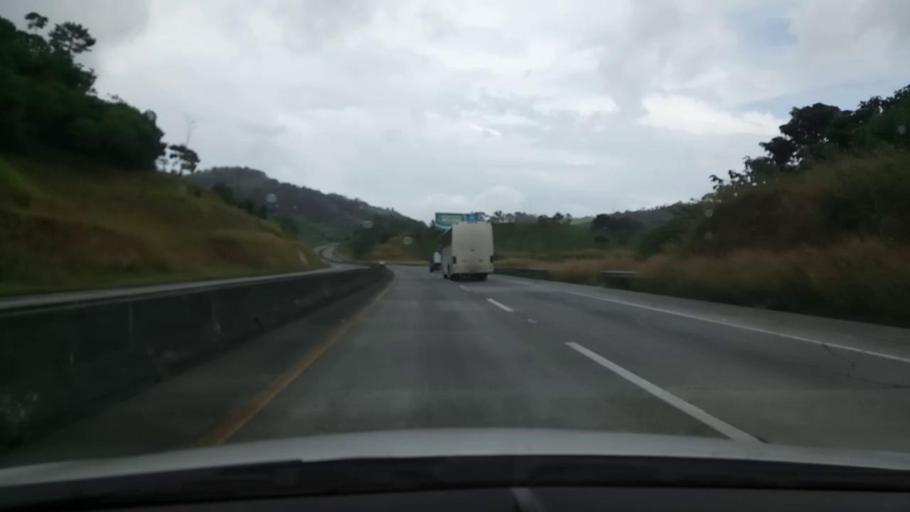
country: PA
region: Colon
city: Gatun
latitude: 9.2805
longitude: -79.7556
